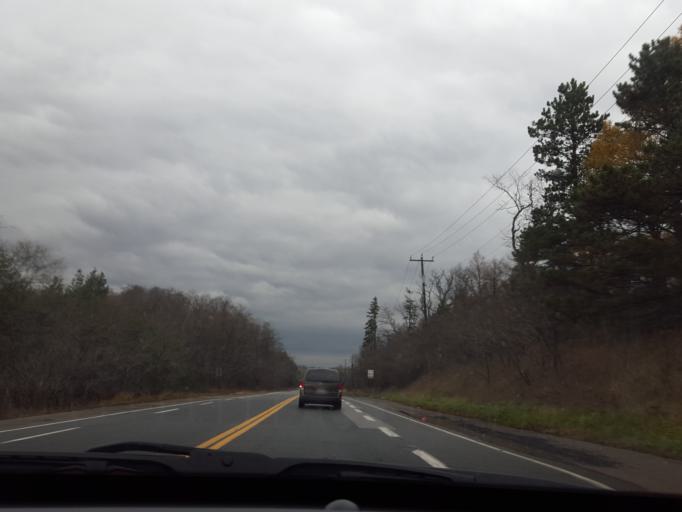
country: CA
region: Ontario
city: Pickering
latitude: 43.8902
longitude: -79.0923
